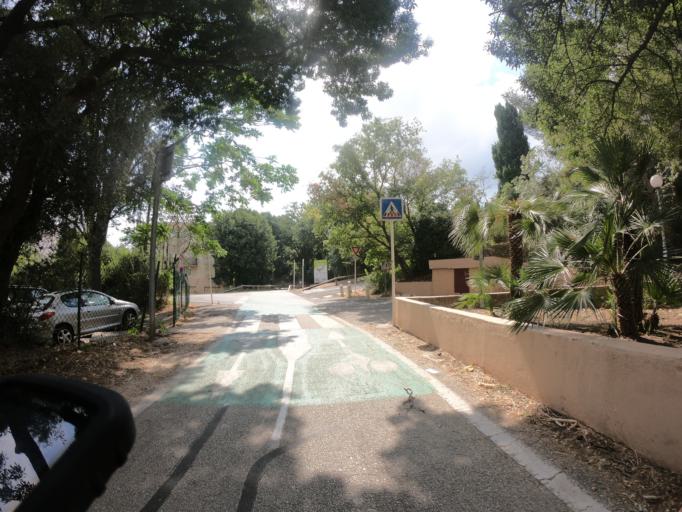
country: FR
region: Provence-Alpes-Cote d'Azur
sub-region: Departement du Var
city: La Valette-du-Var
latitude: 43.1223
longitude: 5.9632
